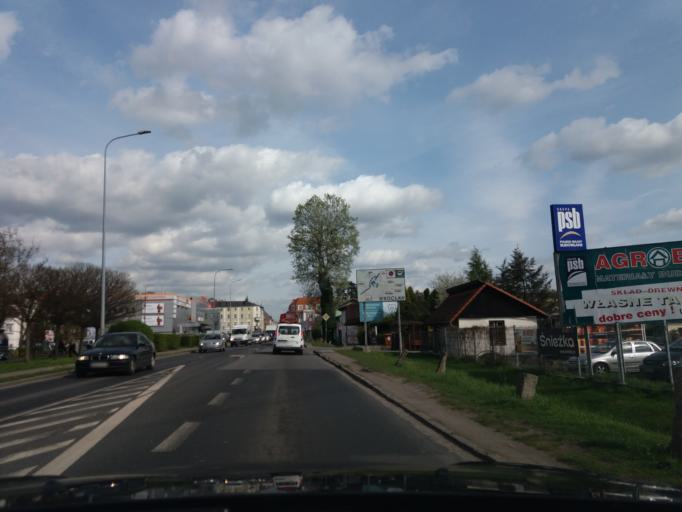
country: PL
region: Lower Silesian Voivodeship
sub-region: Powiat wroclawski
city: Smolec
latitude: 51.1462
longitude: 16.8640
